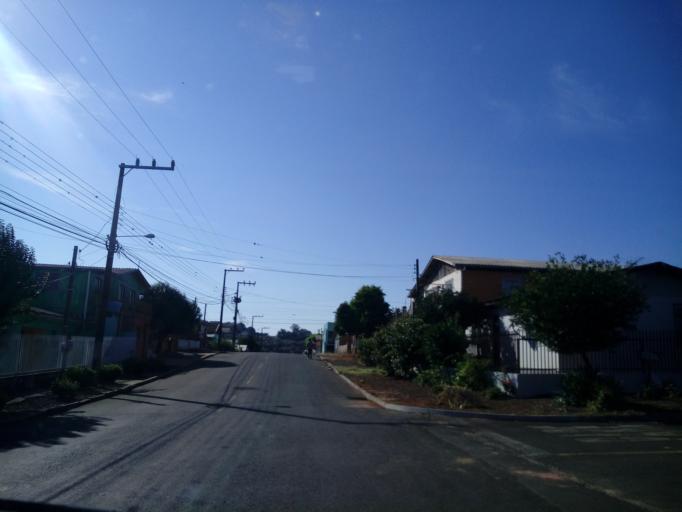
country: BR
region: Santa Catarina
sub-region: Chapeco
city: Chapeco
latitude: -27.0984
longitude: -52.6679
